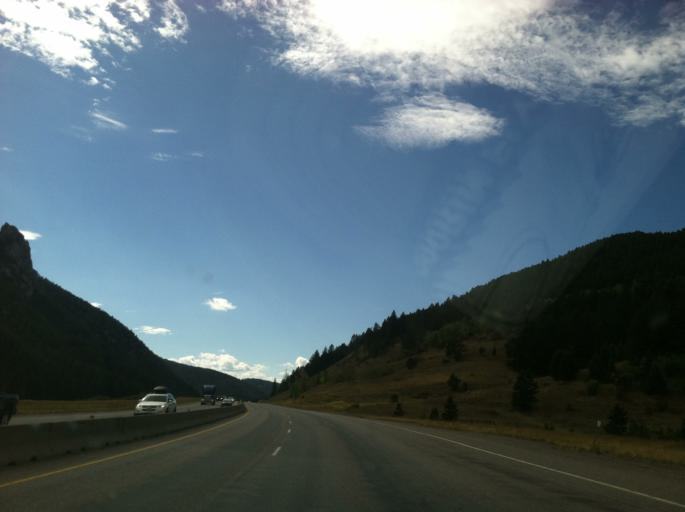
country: US
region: Montana
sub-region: Gallatin County
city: Bozeman
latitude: 45.6466
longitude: -110.8904
